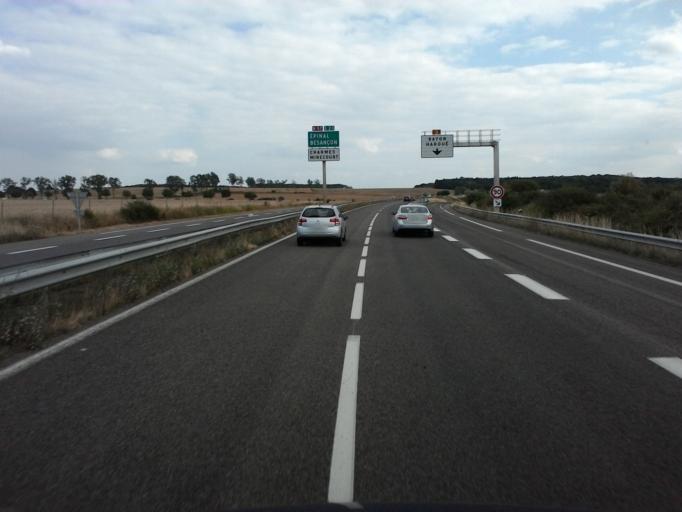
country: FR
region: Lorraine
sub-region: Departement de Meurthe-et-Moselle
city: Bayon
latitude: 48.4729
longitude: 6.2486
